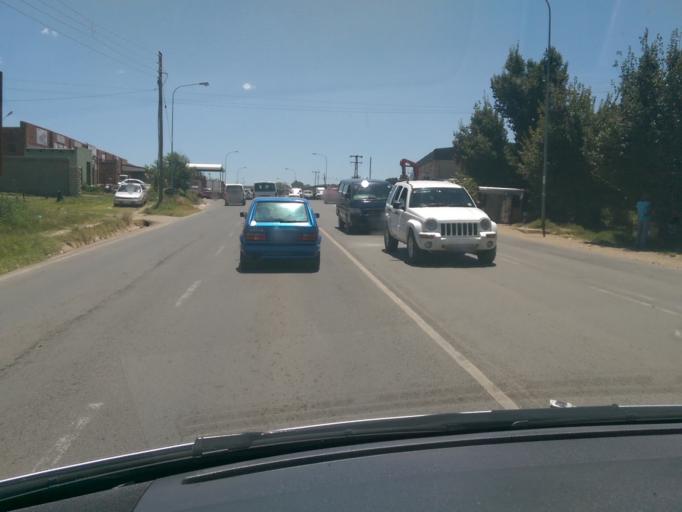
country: LS
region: Maseru
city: Maseru
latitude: -29.3429
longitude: 27.5151
